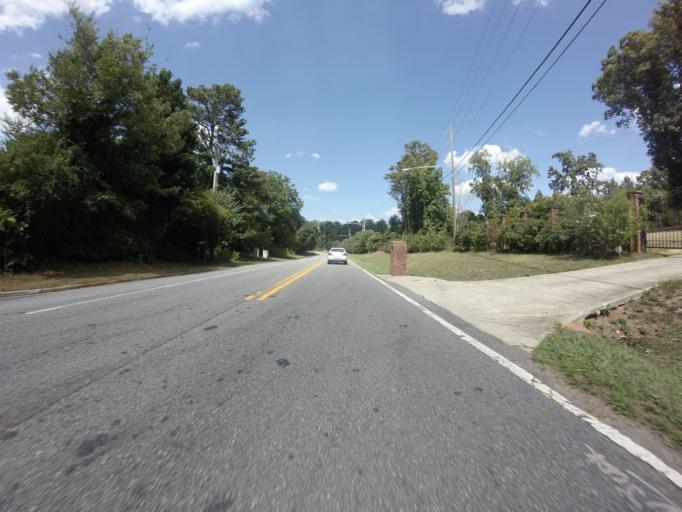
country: US
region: Georgia
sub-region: Fulton County
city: Johns Creek
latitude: 34.0320
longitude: -84.2447
